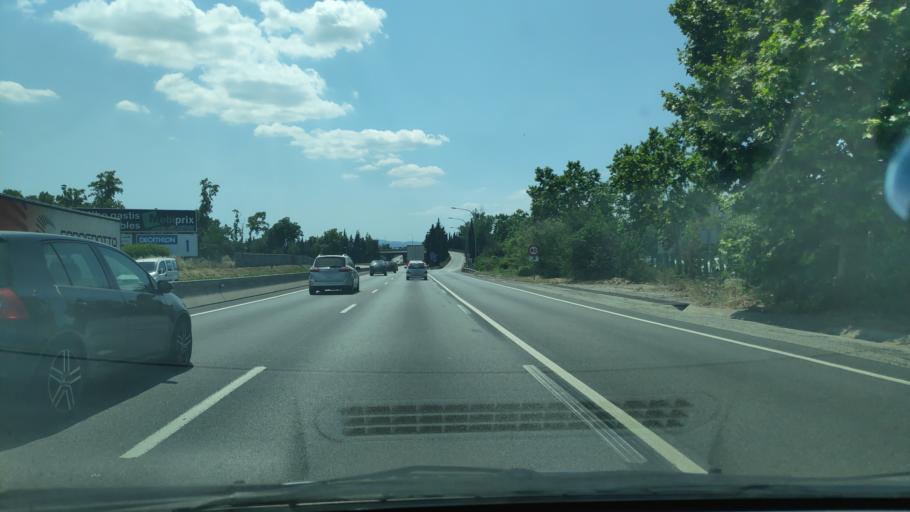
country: ES
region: Catalonia
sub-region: Provincia de Barcelona
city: Parets del Valles
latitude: 41.5656
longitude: 2.2404
